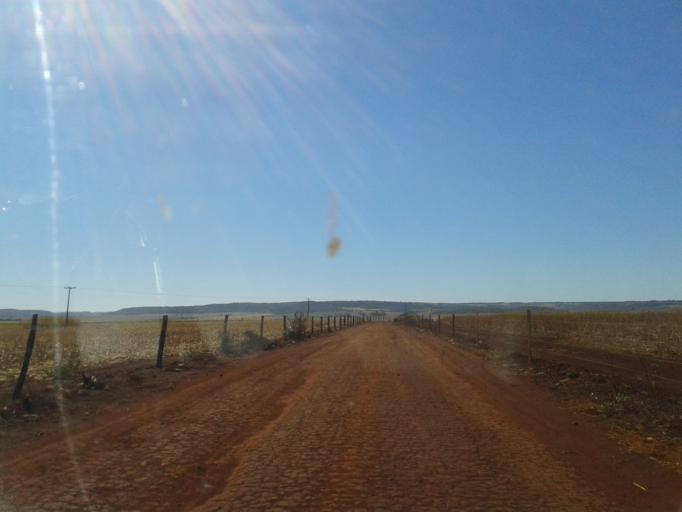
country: BR
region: Minas Gerais
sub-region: Centralina
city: Centralina
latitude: -18.5851
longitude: -49.1389
